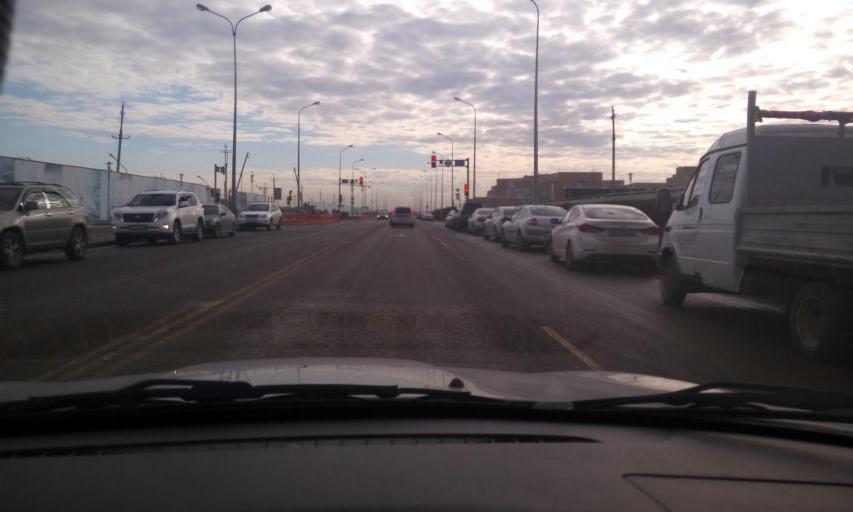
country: KZ
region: Astana Qalasy
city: Astana
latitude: 51.0845
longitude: 71.4148
